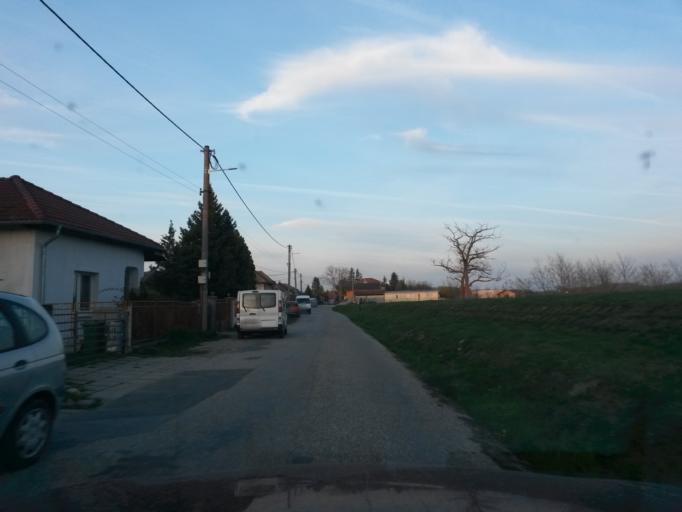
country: HU
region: Komarom-Esztergom
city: Dunaalmas
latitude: 47.7383
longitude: 18.2937
